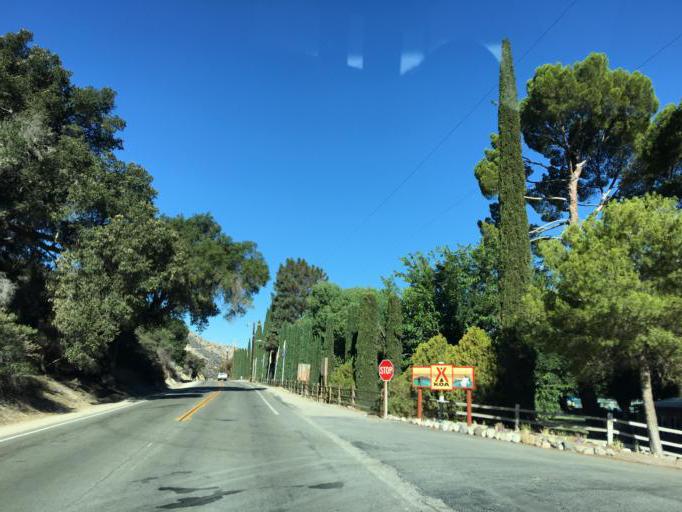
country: US
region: California
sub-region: Los Angeles County
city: Acton
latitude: 34.4376
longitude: -118.2655
